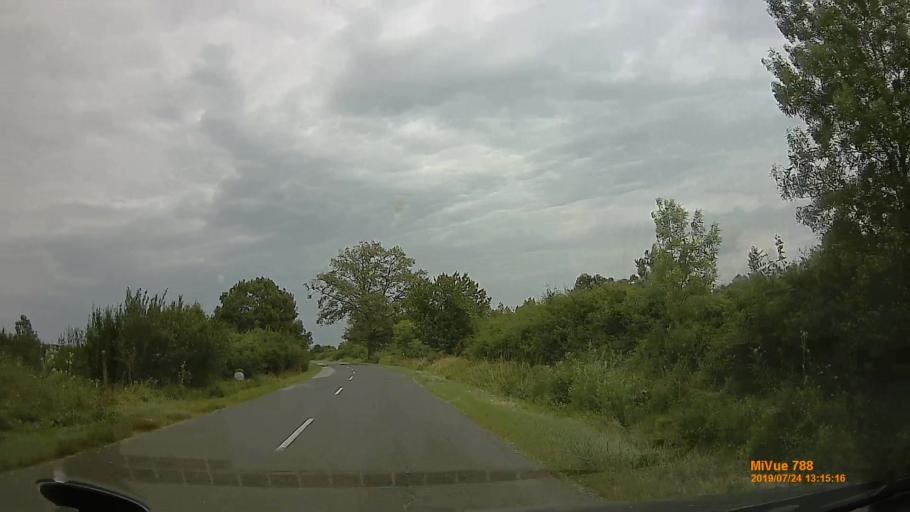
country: HU
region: Szabolcs-Szatmar-Bereg
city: Vasarosnameny
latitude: 48.1890
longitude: 22.3511
